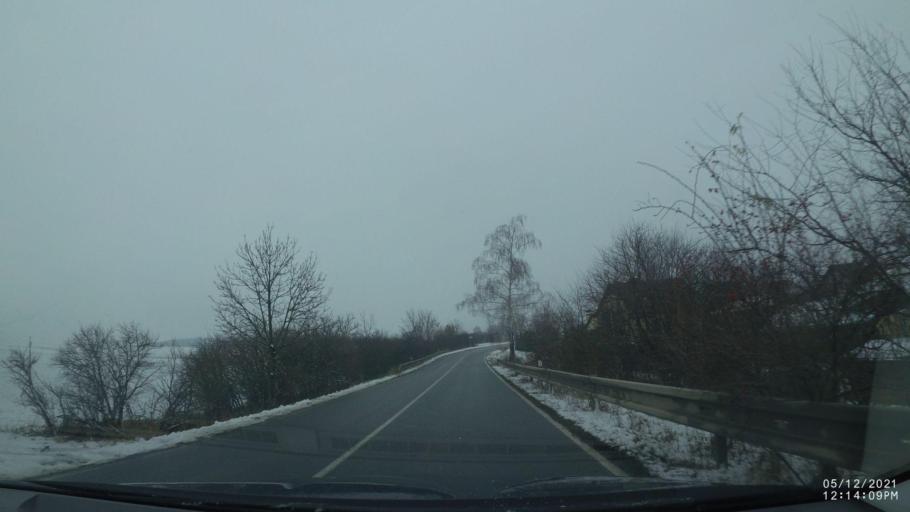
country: CZ
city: Ceske Mezirici
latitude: 50.3059
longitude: 16.0285
